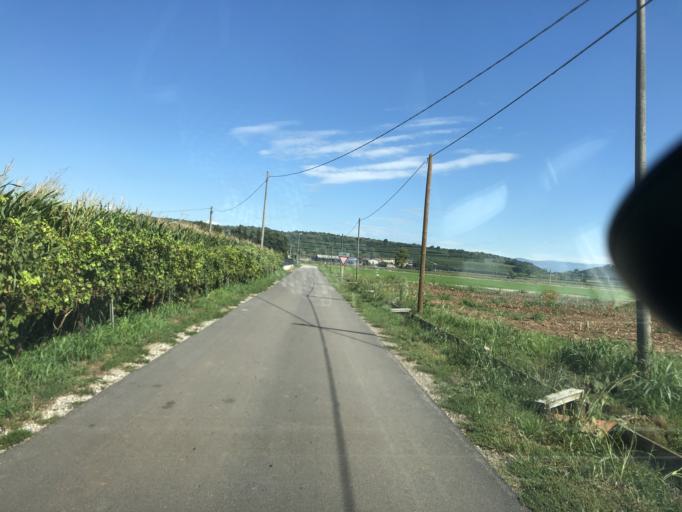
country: IT
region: Veneto
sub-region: Provincia di Verona
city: Quaderni
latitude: 45.3586
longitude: 10.7730
